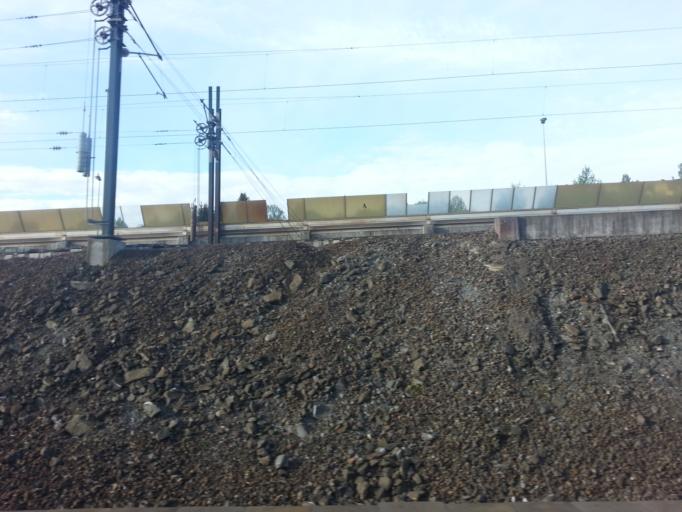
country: NO
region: Akershus
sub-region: Skedsmo
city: Lillestrom
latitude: 59.9525
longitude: 11.0341
